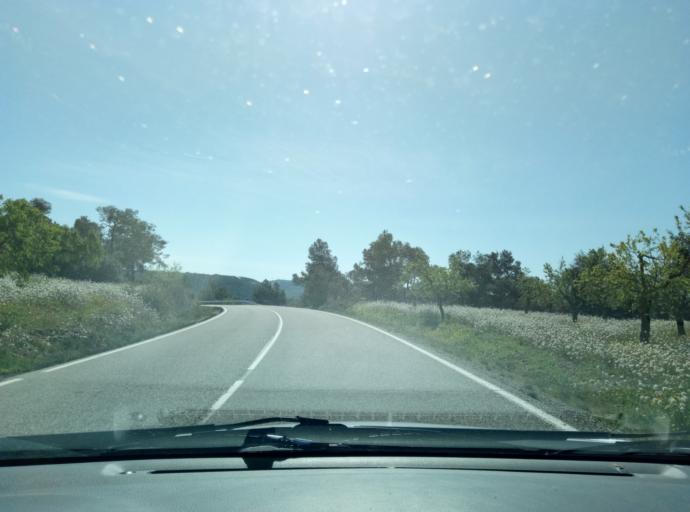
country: ES
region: Catalonia
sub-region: Provincia de Lleida
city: Vallbona de les Monges
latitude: 41.5274
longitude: 1.0258
